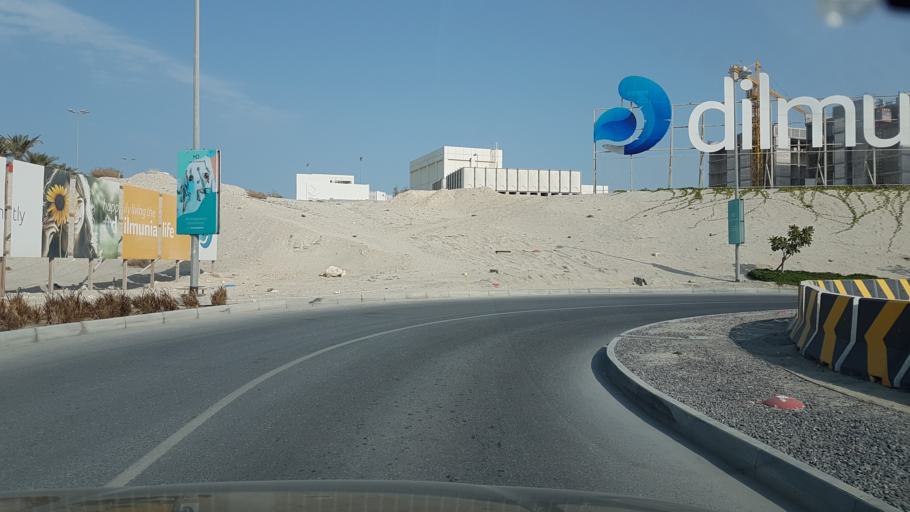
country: BH
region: Muharraq
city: Al Hadd
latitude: 26.2708
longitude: 50.6669
